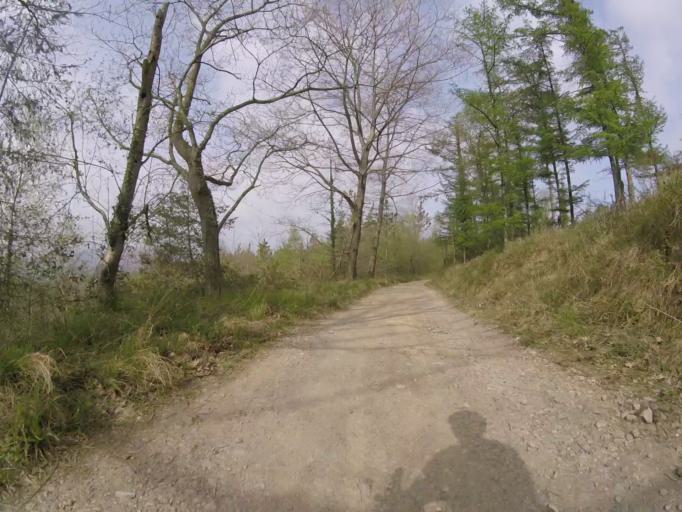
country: ES
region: Basque Country
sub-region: Provincia de Guipuzcoa
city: Usurbil
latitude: 43.2446
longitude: -2.0826
